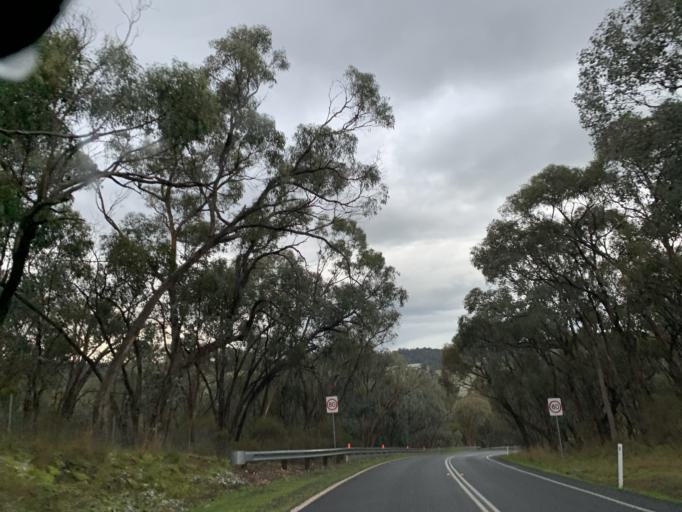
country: AU
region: Victoria
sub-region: Murrindindi
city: Kinglake West
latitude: -37.2192
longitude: 145.1331
